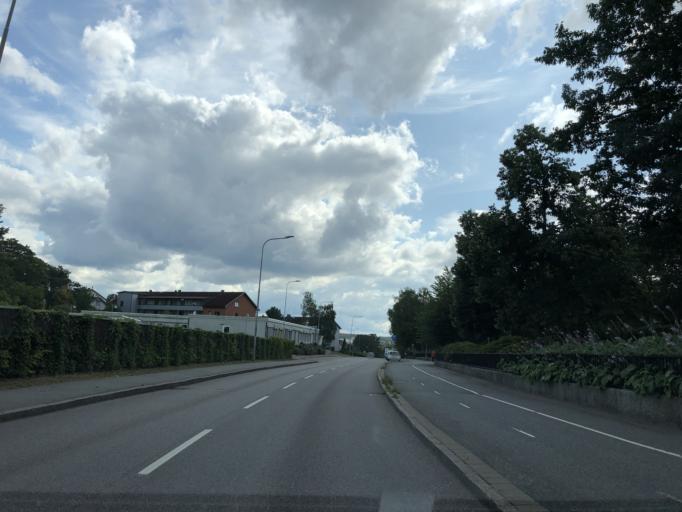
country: SE
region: Vaestra Goetaland
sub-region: Goteborg
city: Majorna
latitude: 57.7145
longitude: 11.9143
